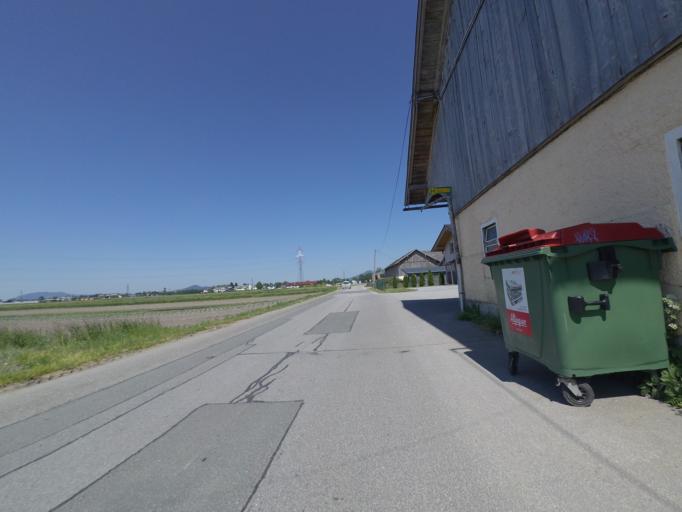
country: DE
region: Bavaria
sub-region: Upper Bavaria
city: Ainring
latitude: 47.7767
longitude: 12.9740
